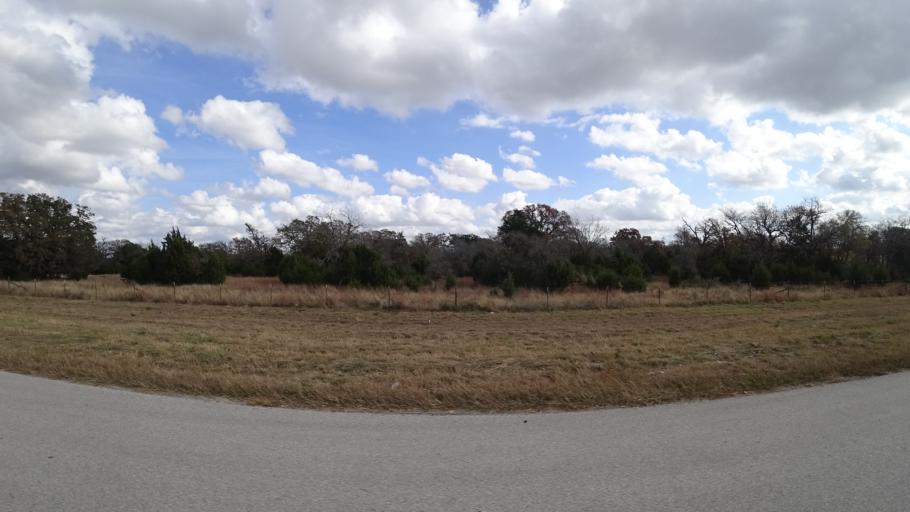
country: US
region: Texas
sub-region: Williamson County
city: Brushy Creek
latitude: 30.4866
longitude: -97.7198
